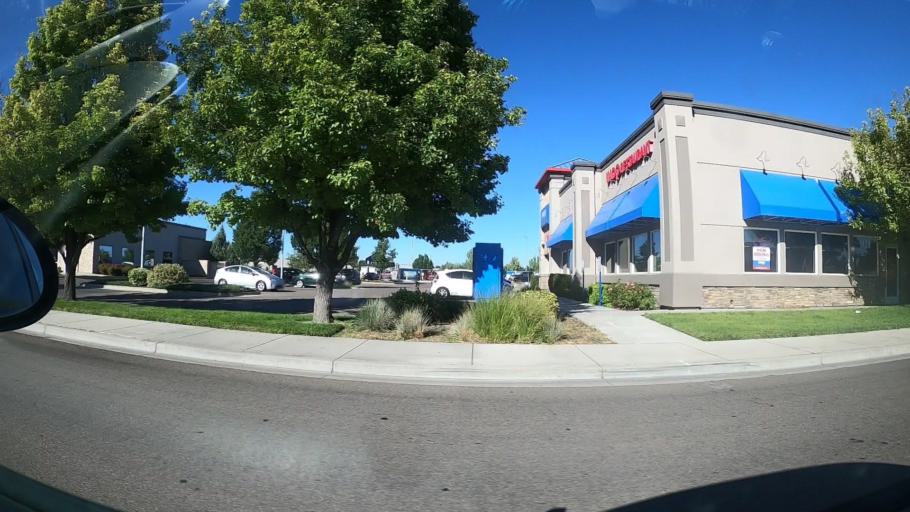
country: US
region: Idaho
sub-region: Canyon County
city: Nampa
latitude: 43.6007
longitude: -116.5960
